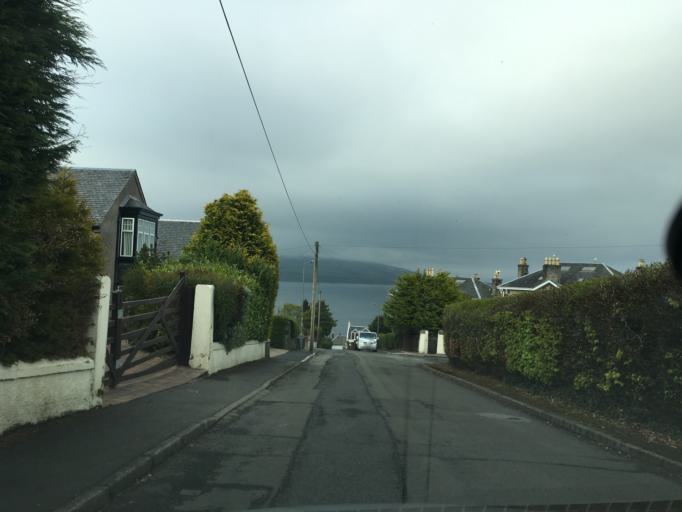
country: GB
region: Scotland
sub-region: Argyll and Bute
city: Rothesay
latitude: 55.8411
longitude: -5.0279
